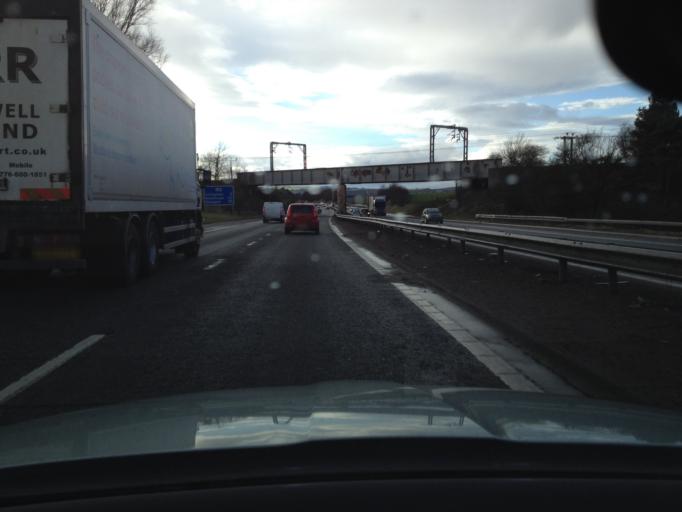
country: GB
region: Scotland
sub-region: Edinburgh
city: Newbridge
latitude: 55.9255
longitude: -3.4288
